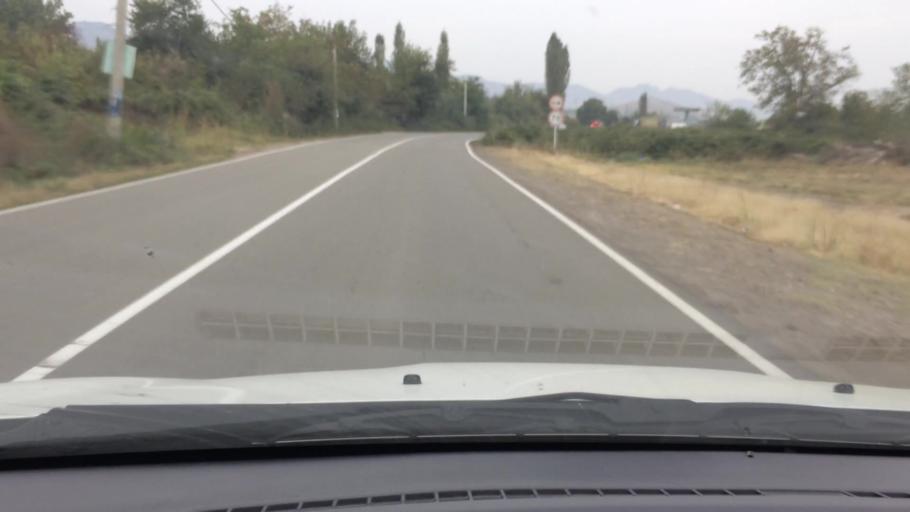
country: AM
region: Tavush
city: Bagratashen
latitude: 41.2627
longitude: 44.7949
